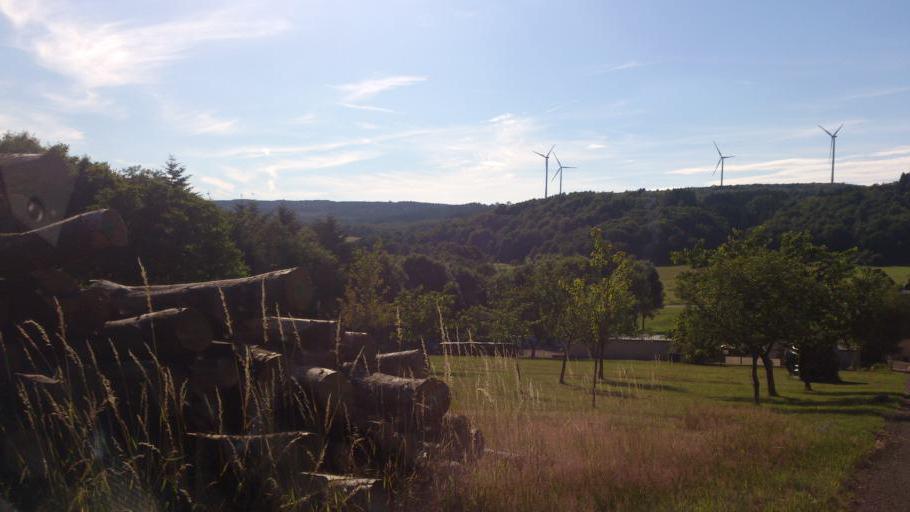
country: DE
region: Rheinland-Pfalz
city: Achtelsbach
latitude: 49.5751
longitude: 7.0685
